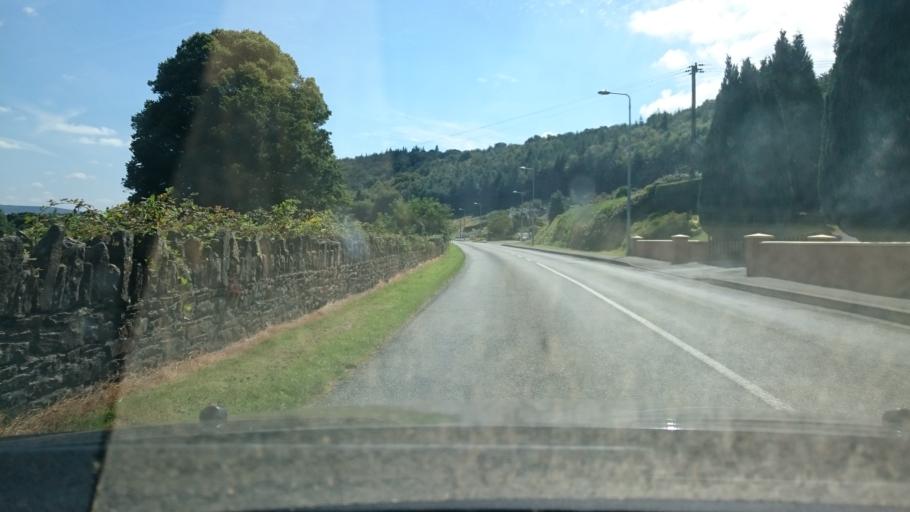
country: IE
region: Leinster
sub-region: Kilkenny
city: Graiguenamanagh
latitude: 52.5361
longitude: -6.9626
